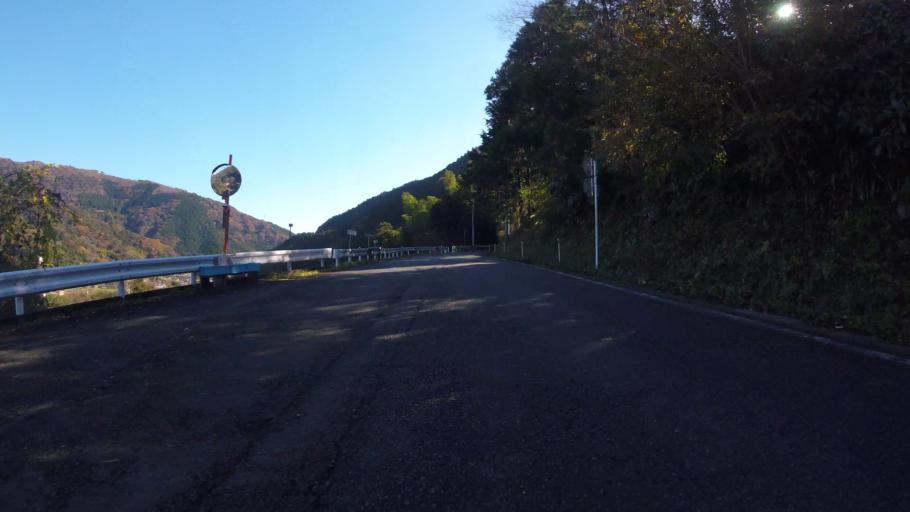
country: JP
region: Shizuoka
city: Shimoda
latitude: 34.7674
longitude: 138.9618
